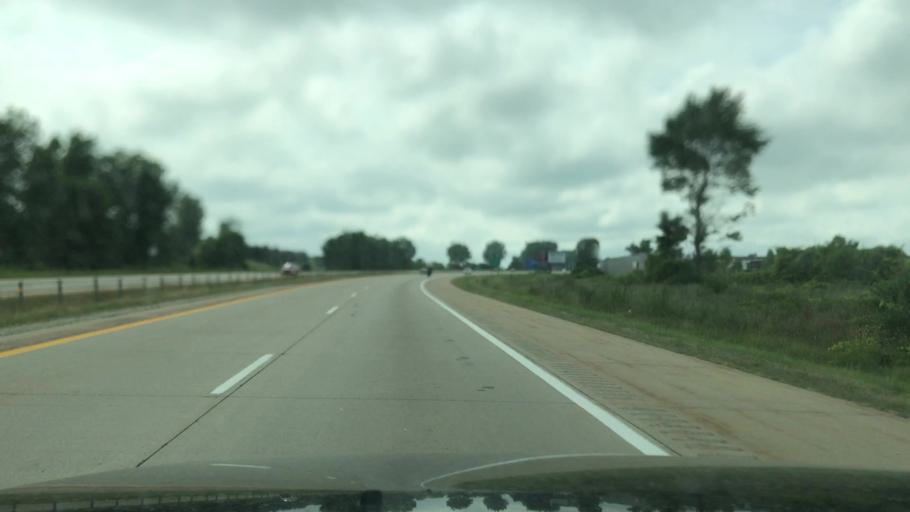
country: US
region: Michigan
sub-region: Ottawa County
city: Coopersville
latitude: 43.0528
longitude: -85.9449
